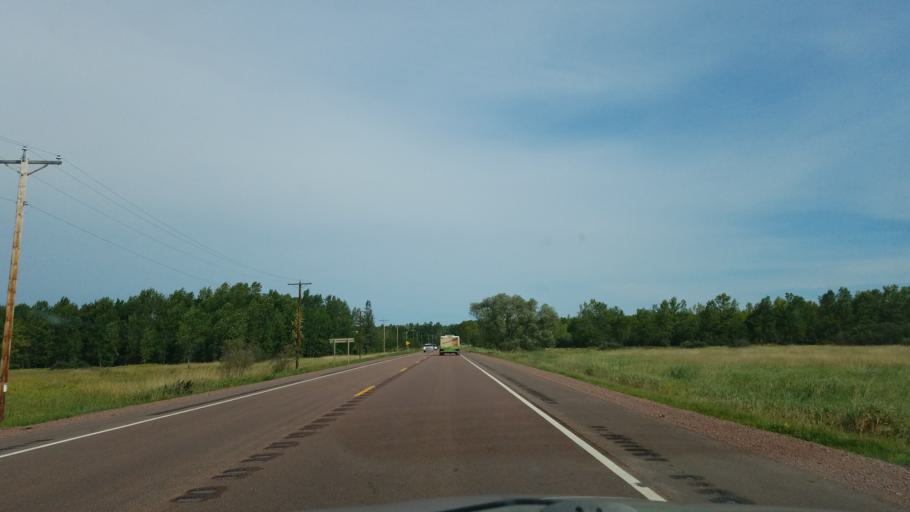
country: US
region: Wisconsin
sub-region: Ashland County
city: Ashland
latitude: 46.5956
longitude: -90.9551
